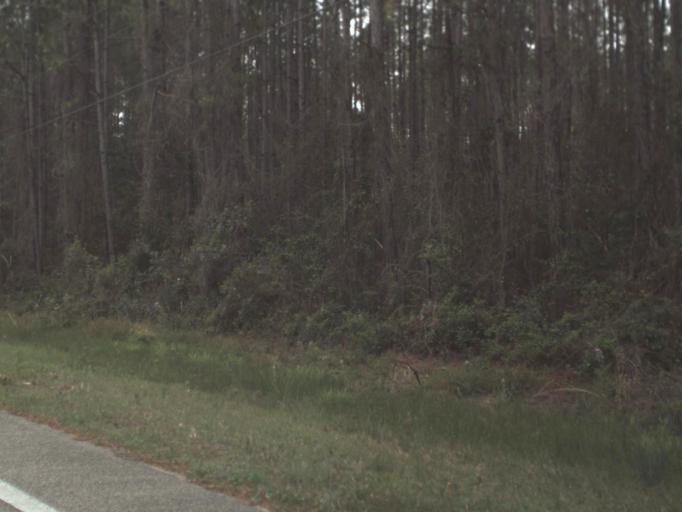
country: US
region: Florida
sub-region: Gulf County
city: Port Saint Joe
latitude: 29.8431
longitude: -85.2663
